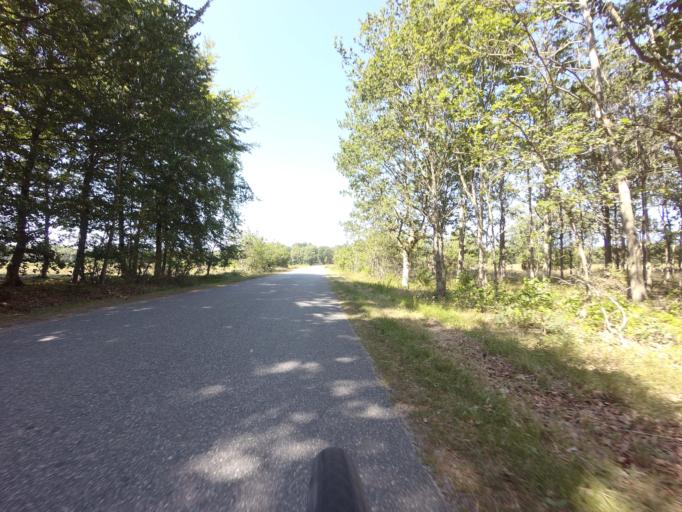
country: DK
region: North Denmark
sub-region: Laeso Kommune
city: Byrum
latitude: 57.2786
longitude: 11.0100
